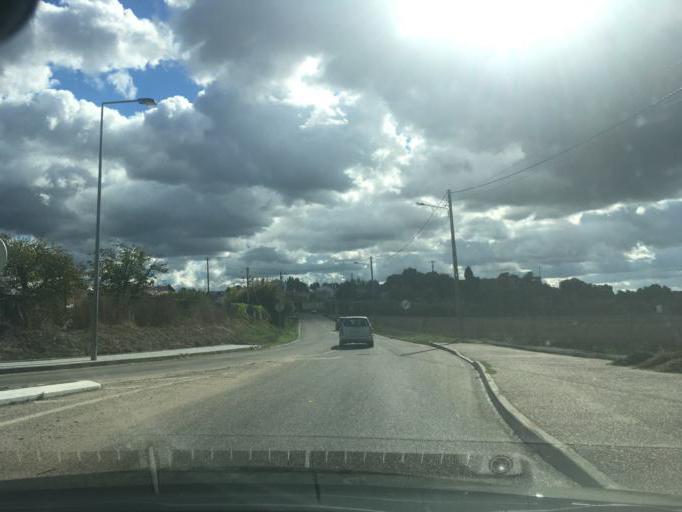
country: PT
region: Santarem
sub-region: Torres Novas
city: Riachos
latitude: 39.4514
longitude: -8.5185
